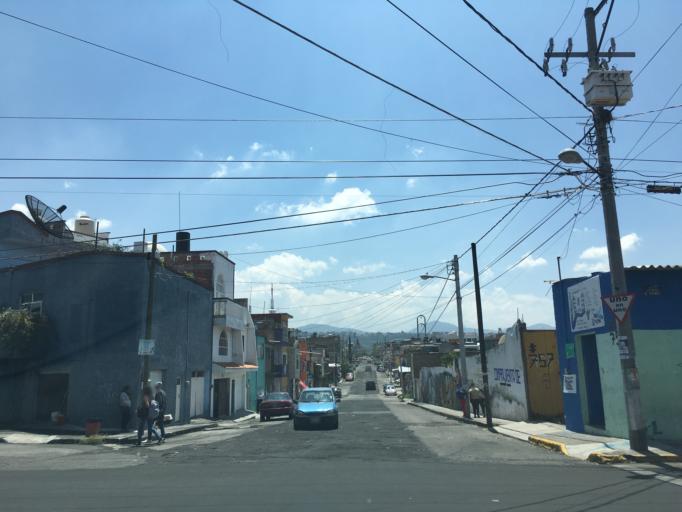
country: MX
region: Michoacan
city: Morelia
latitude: 19.7050
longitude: -101.1726
